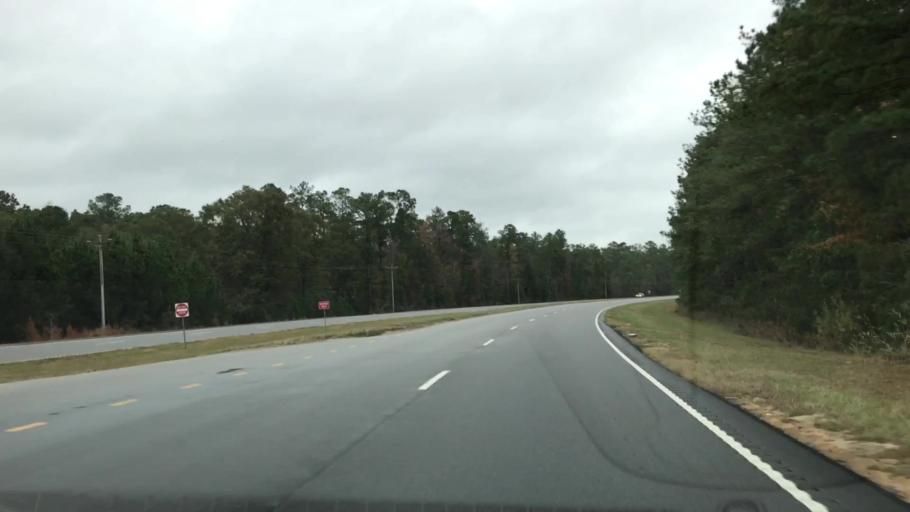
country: US
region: South Carolina
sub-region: Georgetown County
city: Georgetown
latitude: 33.2497
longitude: -79.3750
